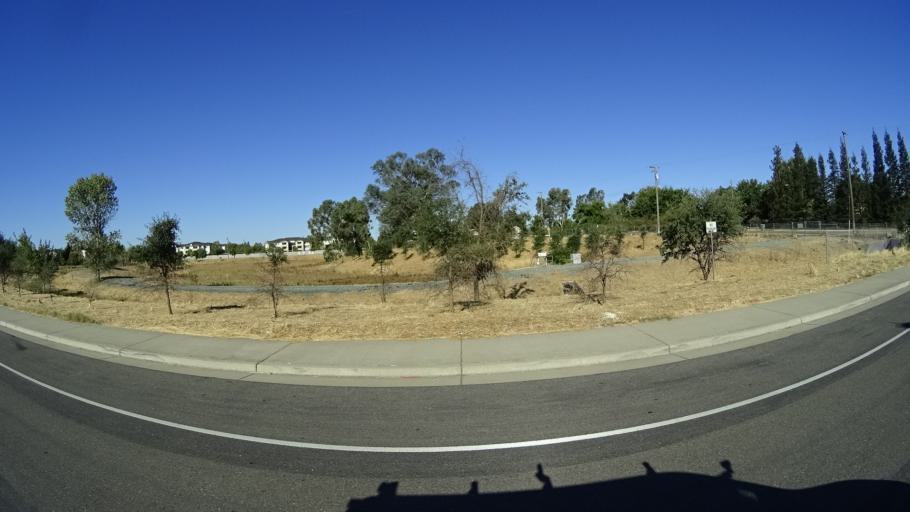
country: US
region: California
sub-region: Sacramento County
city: Vineyard
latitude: 38.4483
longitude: -121.3666
